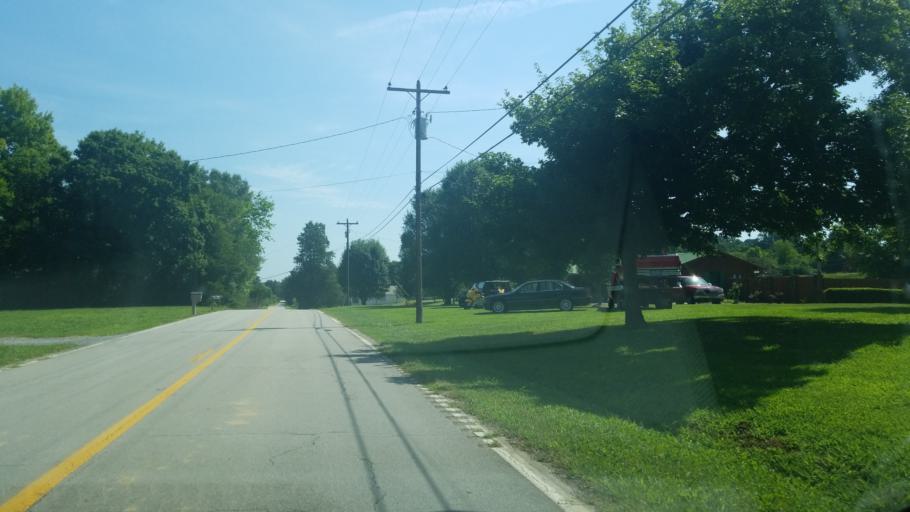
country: US
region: Tennessee
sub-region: Hamilton County
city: Sale Creek
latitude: 35.3227
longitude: -85.0200
